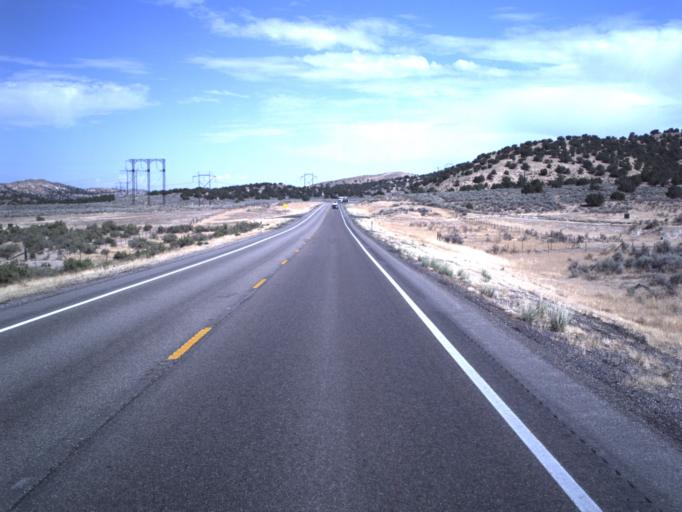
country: US
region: Utah
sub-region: Sanpete County
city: Gunnison
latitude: 39.3464
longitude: -111.9258
